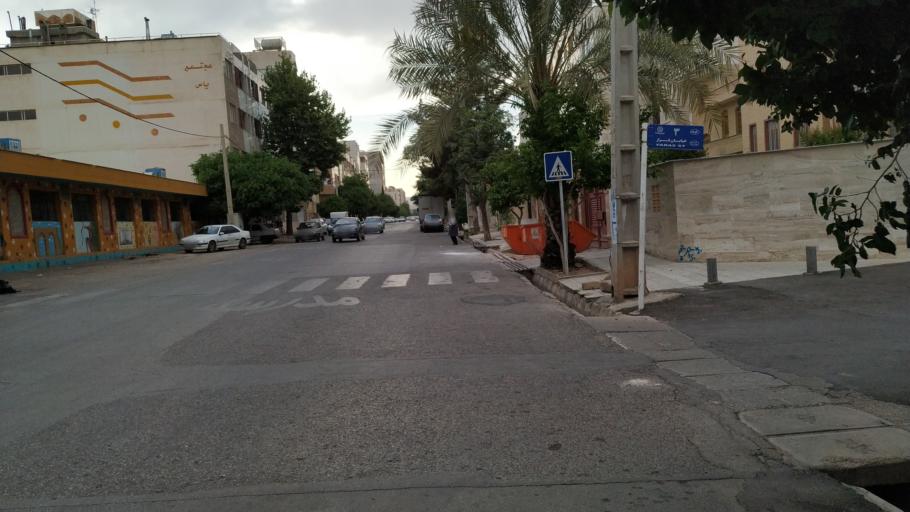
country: IR
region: Fars
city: Shiraz
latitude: 29.6083
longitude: 52.4897
